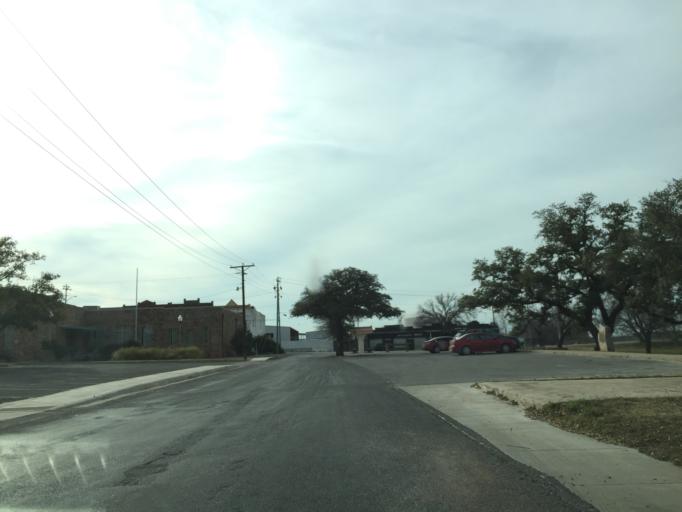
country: US
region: Texas
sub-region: Llano County
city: Llano
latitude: 30.7513
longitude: -98.6748
